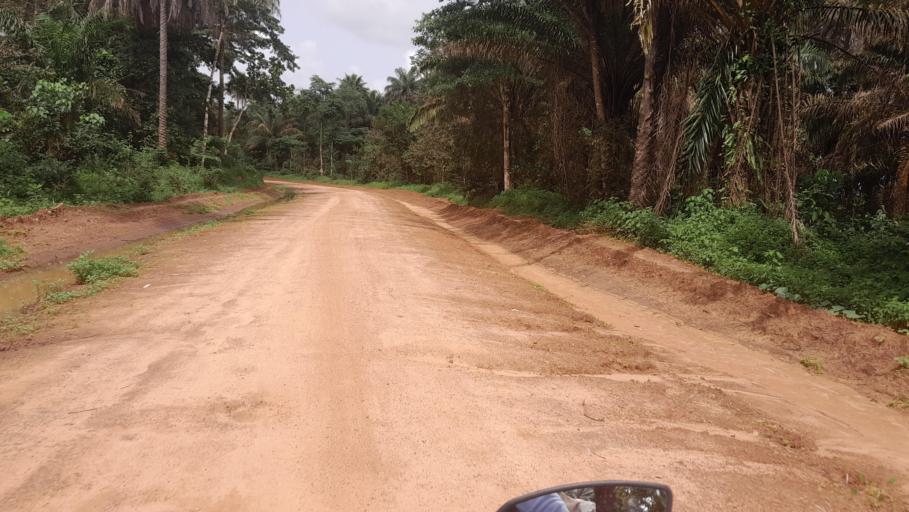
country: GN
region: Boke
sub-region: Boffa
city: Boffa
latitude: 10.0870
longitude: -13.8642
